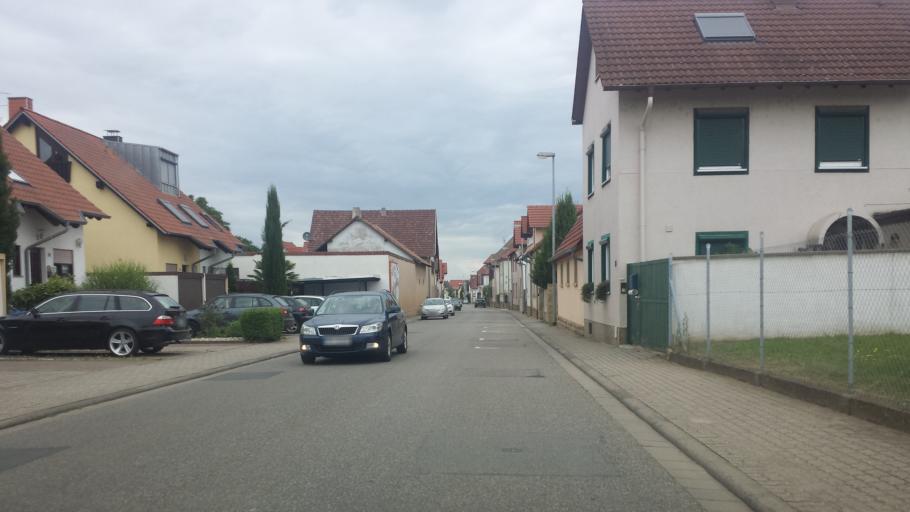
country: DE
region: Rheinland-Pfalz
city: Meckenheim
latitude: 49.4006
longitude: 8.2424
